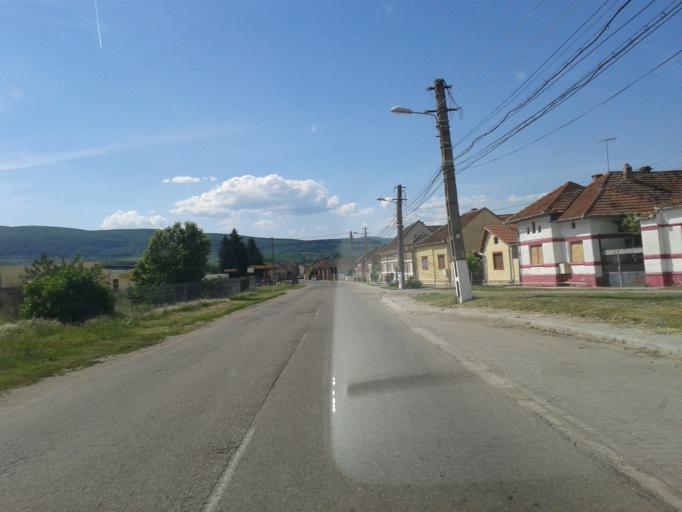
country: RO
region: Hunedoara
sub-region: Comuna Geoagiu
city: Geoagiu
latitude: 45.9078
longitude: 23.2108
